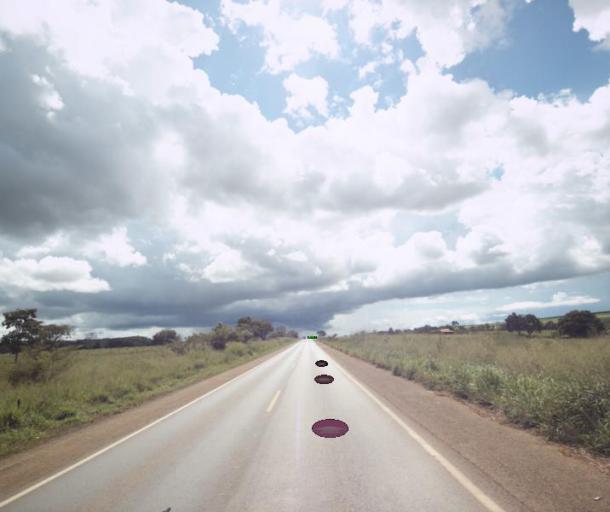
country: BR
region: Goias
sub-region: Uruacu
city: Uruacu
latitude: -14.7047
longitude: -49.1023
